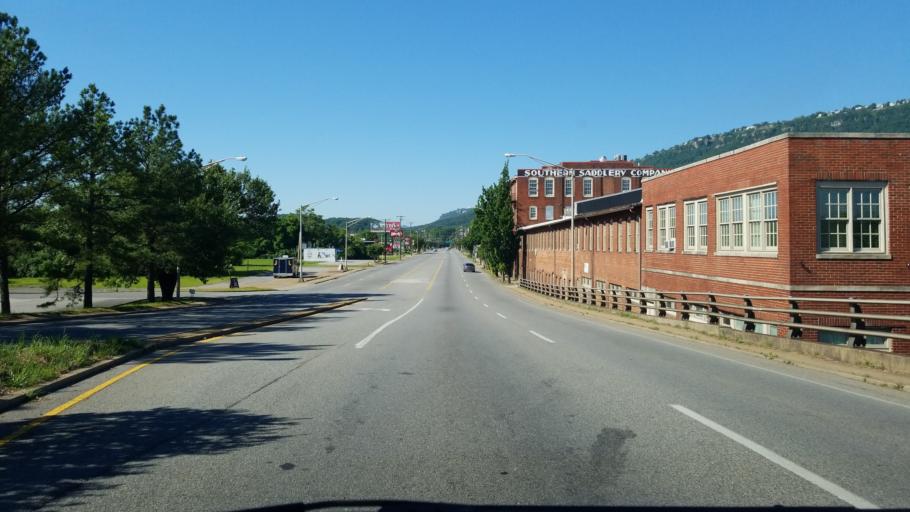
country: US
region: Tennessee
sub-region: Hamilton County
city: Chattanooga
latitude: 35.0227
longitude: -85.3195
